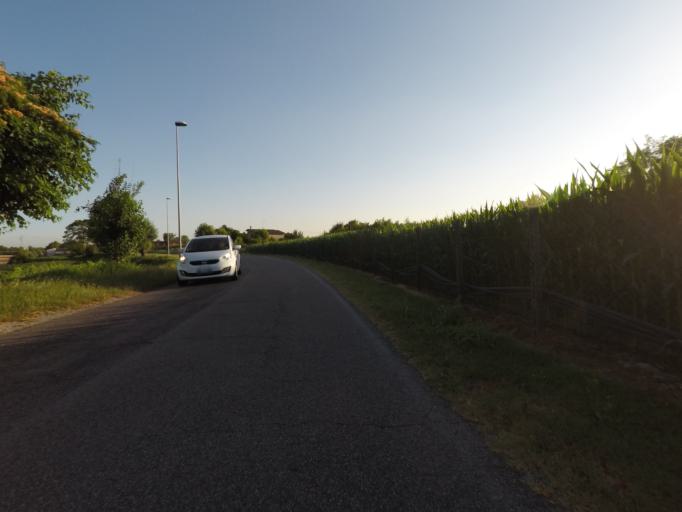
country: IT
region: Veneto
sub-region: Provincia di Rovigo
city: Fratta Polesine
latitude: 45.0432
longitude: 11.6472
